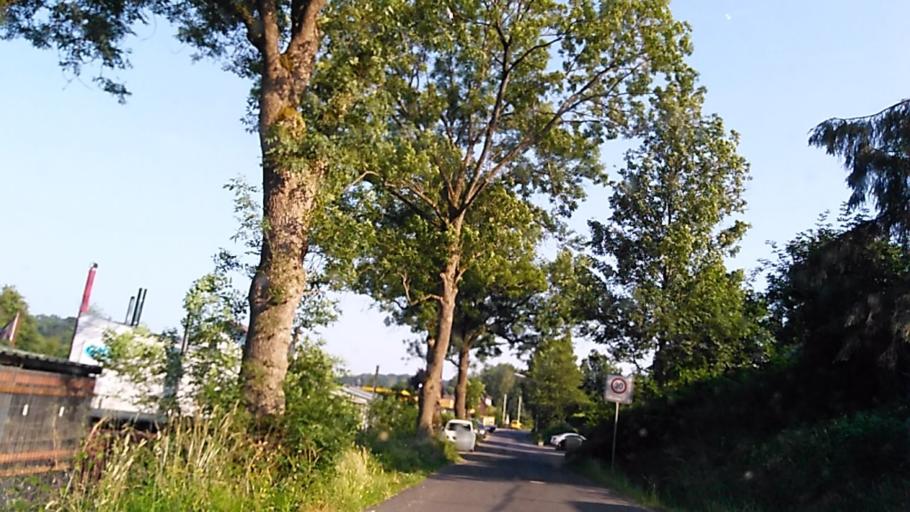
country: DE
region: North Rhine-Westphalia
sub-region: Regierungsbezirk Koln
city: Much
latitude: 50.9094
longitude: 7.4059
